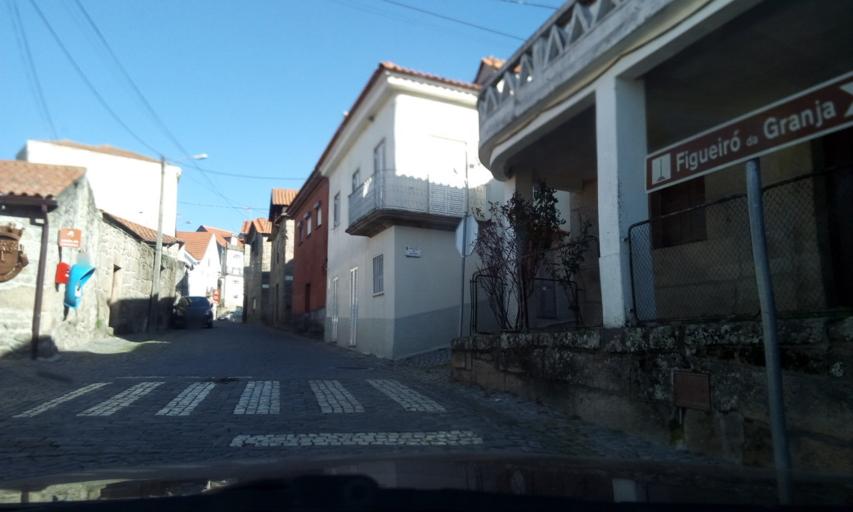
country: PT
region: Guarda
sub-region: Fornos de Algodres
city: Fornos de Algodres
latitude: 40.6278
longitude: -7.4995
